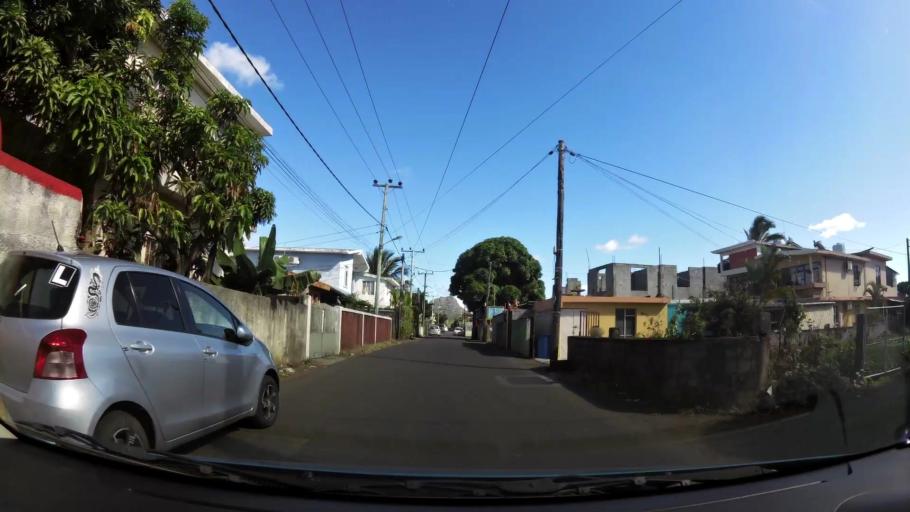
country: MU
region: Plaines Wilhems
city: Vacoas
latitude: -20.2809
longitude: 57.4671
